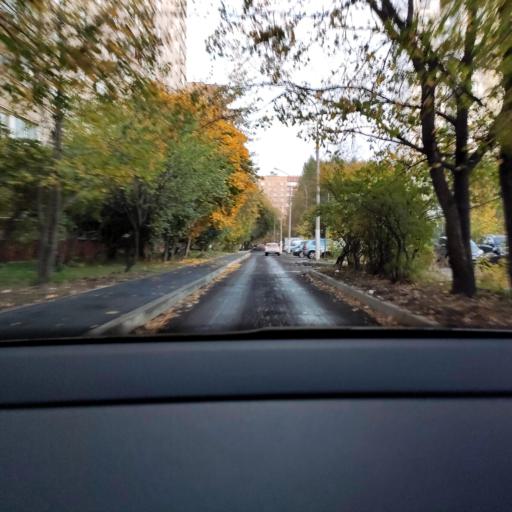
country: RU
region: Moscow
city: Slobodka
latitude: 55.8672
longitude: 37.5898
